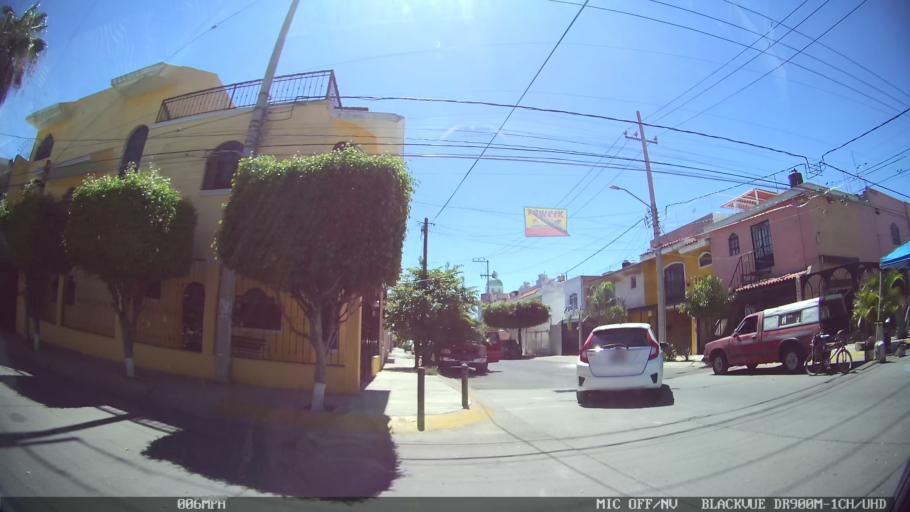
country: MX
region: Jalisco
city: Tlaquepaque
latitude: 20.6643
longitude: -103.2854
